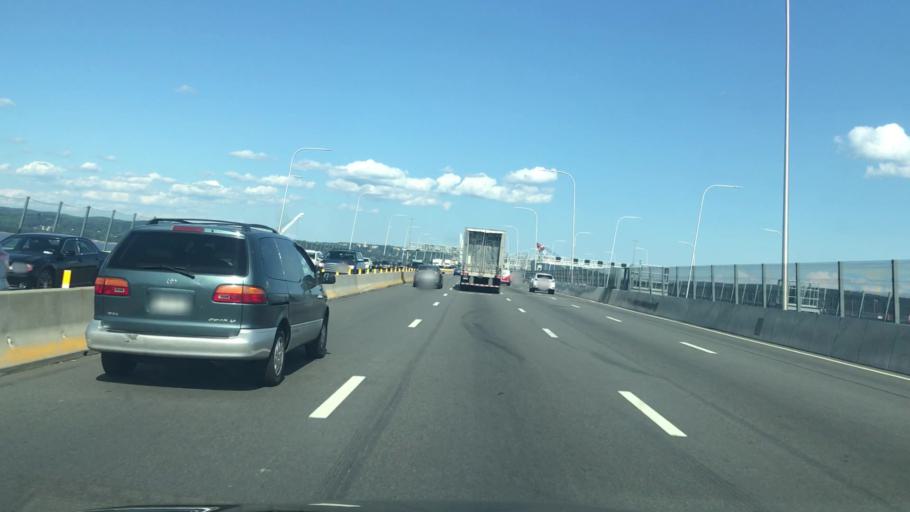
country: US
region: New York
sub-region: Rockland County
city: South Nyack
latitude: 41.0719
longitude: -73.9115
